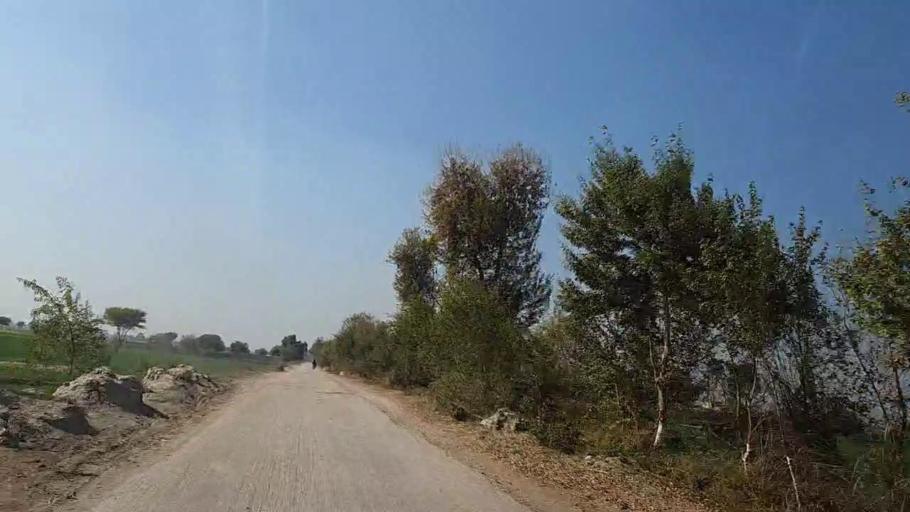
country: PK
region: Sindh
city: Daulatpur
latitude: 26.2905
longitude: 68.0761
